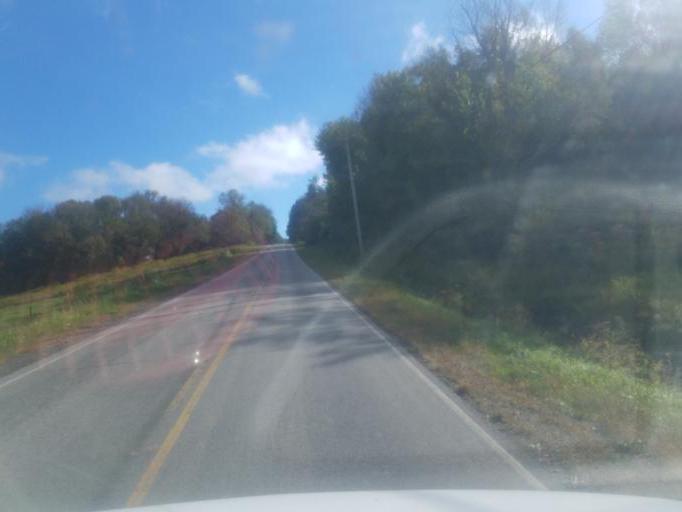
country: US
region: New York
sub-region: Allegany County
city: Friendship
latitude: 42.2758
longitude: -78.1938
